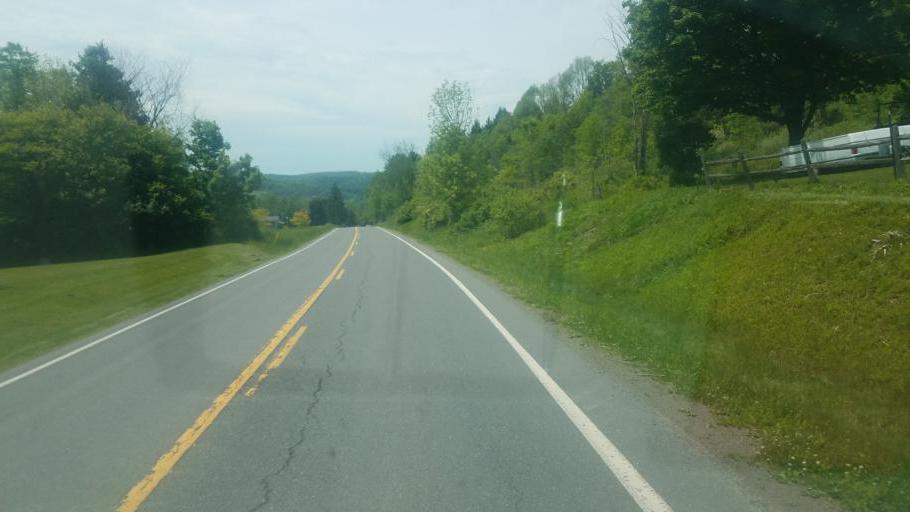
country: US
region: Pennsylvania
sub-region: Tioga County
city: Wellsboro
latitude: 41.7581
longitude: -77.2698
